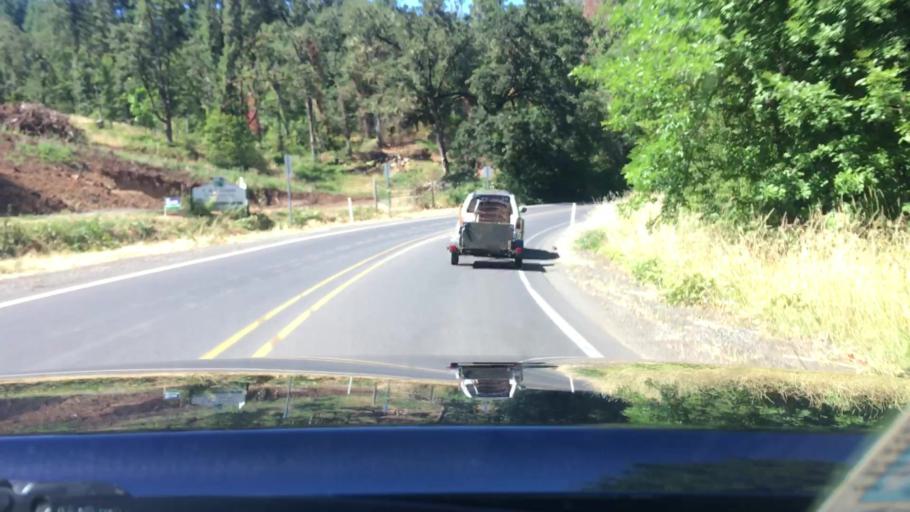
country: US
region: Oregon
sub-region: Lane County
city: Cottage Grove
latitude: 43.8209
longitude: -123.0469
